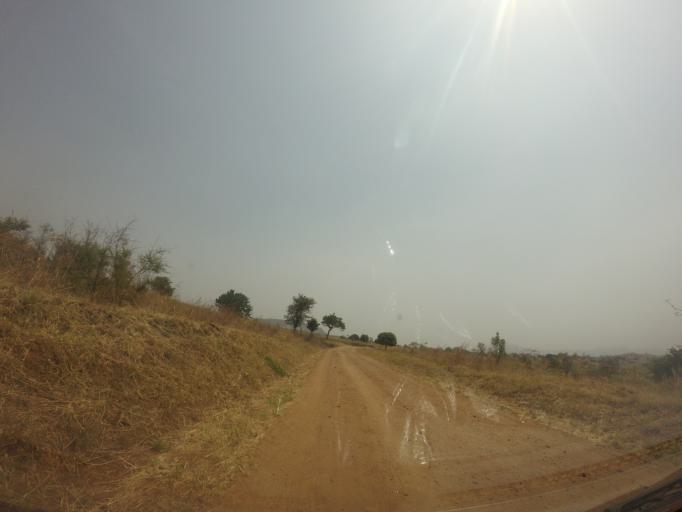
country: UG
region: Northern Region
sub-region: Arua District
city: Arua
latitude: 2.9241
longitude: 30.9940
